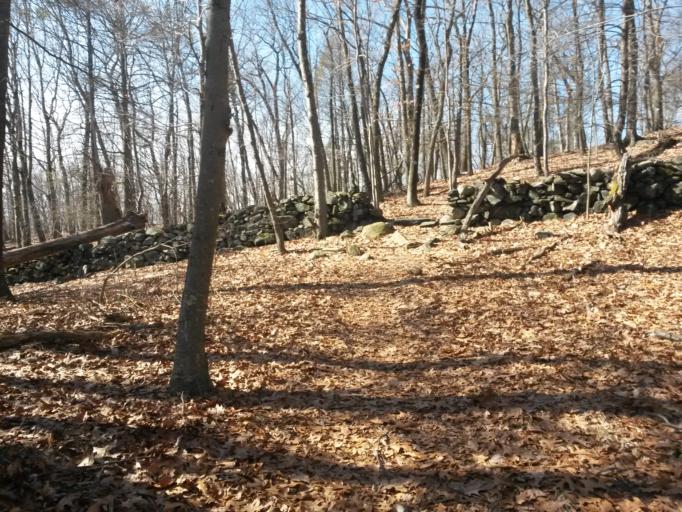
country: US
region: New York
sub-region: Westchester County
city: Yorktown Heights
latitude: 41.2552
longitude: -73.7667
